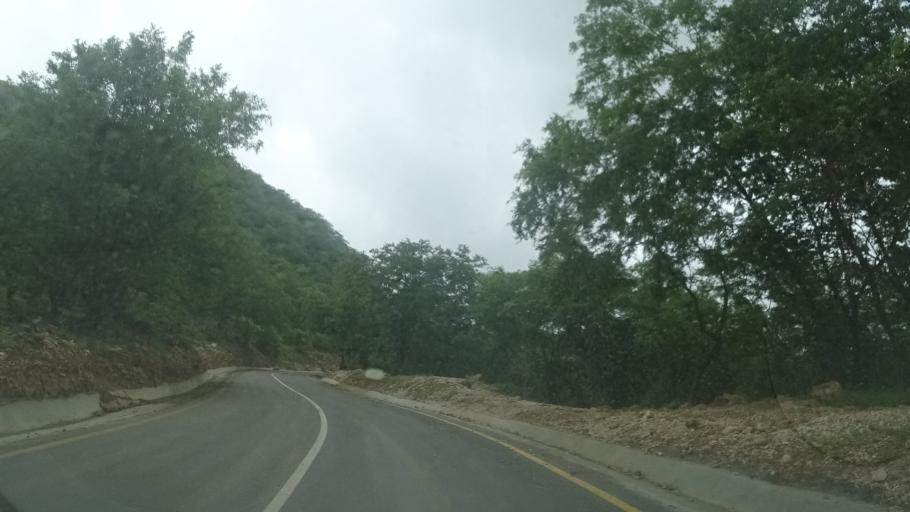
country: OM
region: Zufar
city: Salalah
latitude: 17.1073
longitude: 54.3586
